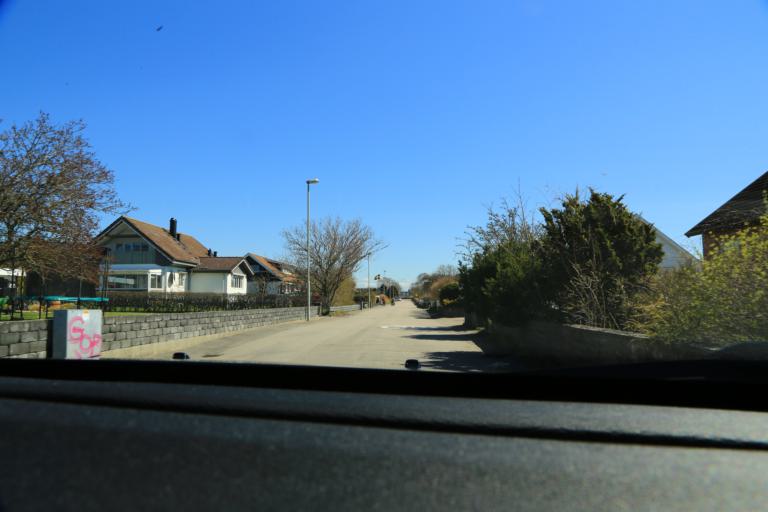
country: SE
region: Halland
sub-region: Varbergs Kommun
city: Traslovslage
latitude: 57.0550
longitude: 12.2807
